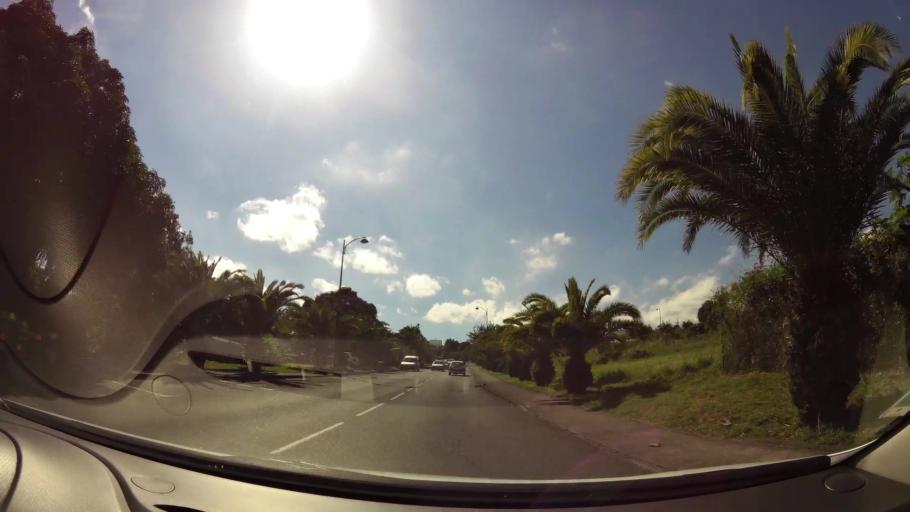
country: RE
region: Reunion
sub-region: Reunion
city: Le Tampon
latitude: -21.2803
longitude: 55.5015
